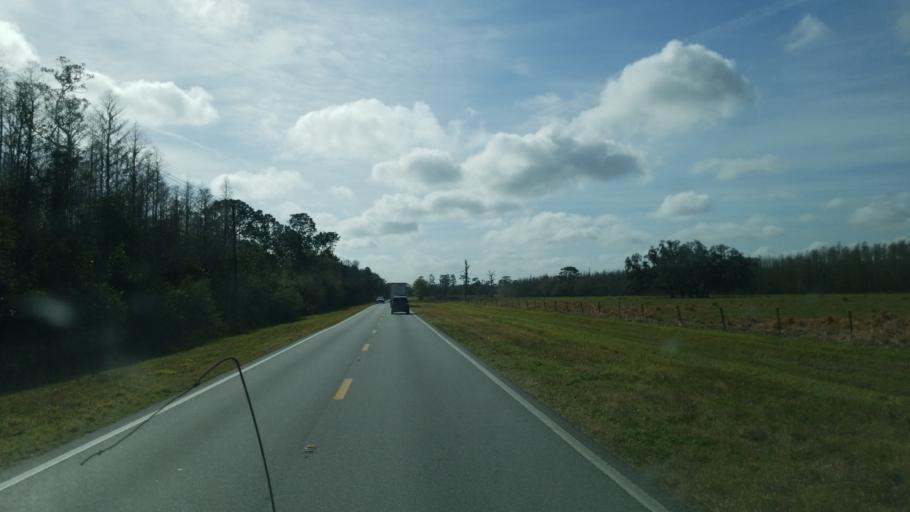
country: US
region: Florida
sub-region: Polk County
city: Polk City
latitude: 28.2426
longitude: -81.7585
